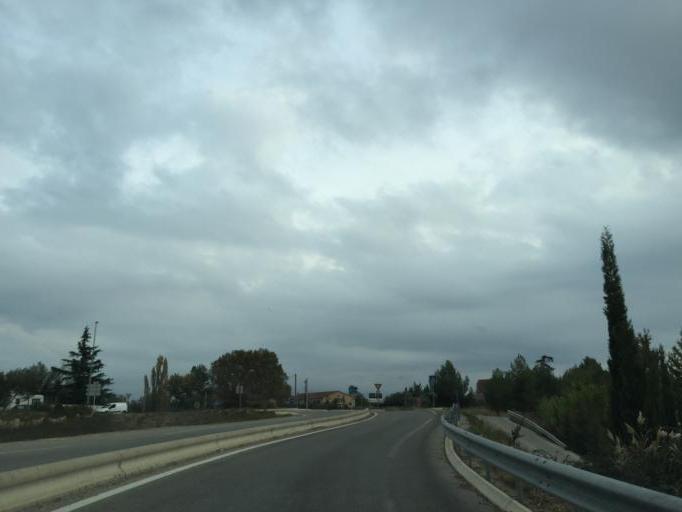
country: FR
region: Languedoc-Roussillon
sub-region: Departement du Gard
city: Remoulins
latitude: 43.9551
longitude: 4.5661
